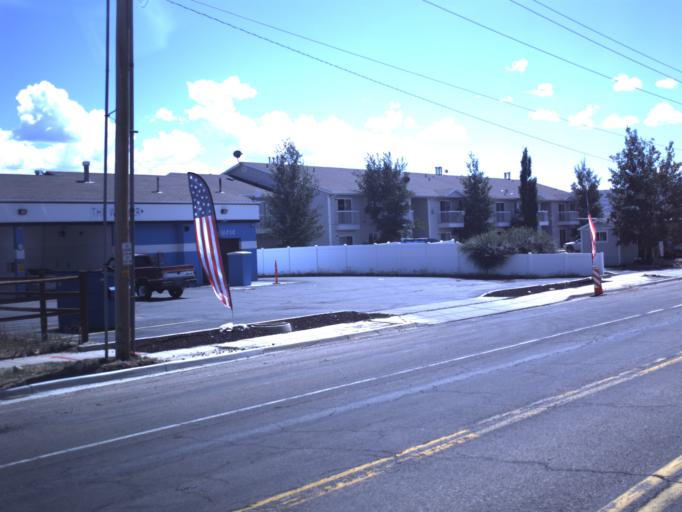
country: US
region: Utah
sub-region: Summit County
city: Kamas
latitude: 40.6342
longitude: -111.2808
